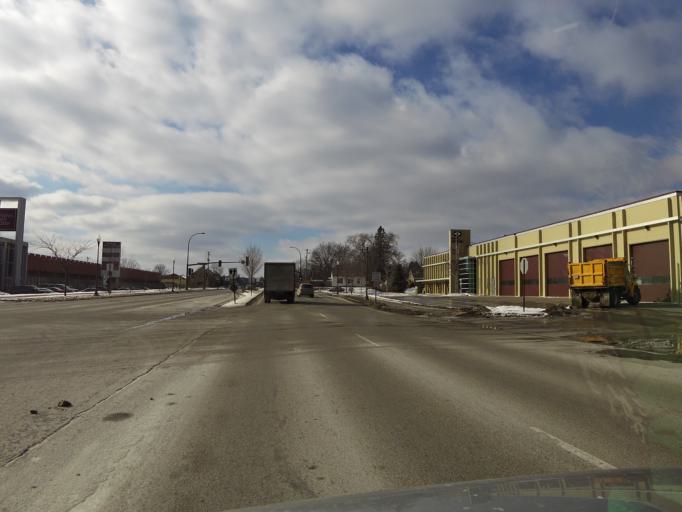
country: US
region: Minnesota
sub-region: Hennepin County
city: Minnetonka Mills
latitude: 44.9209
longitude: -93.4203
